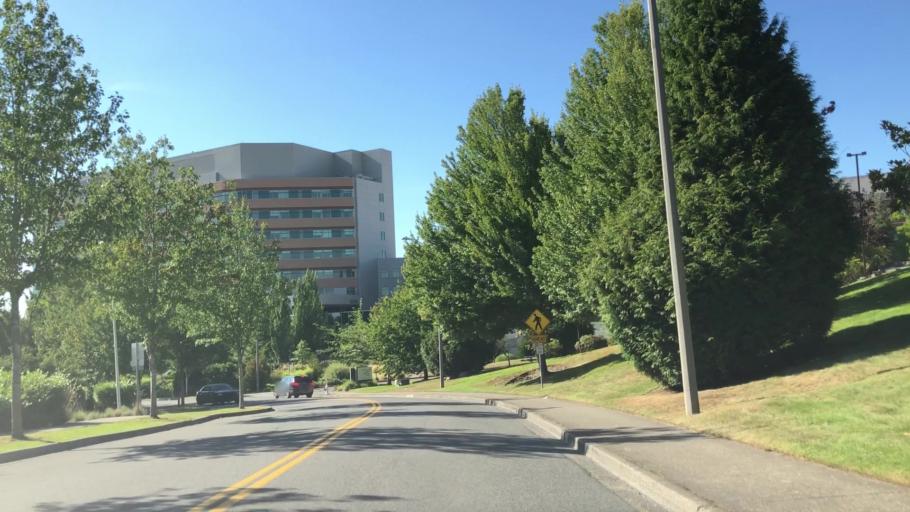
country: US
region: Washington
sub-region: King County
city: Kingsgate
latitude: 47.7144
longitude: -122.1778
